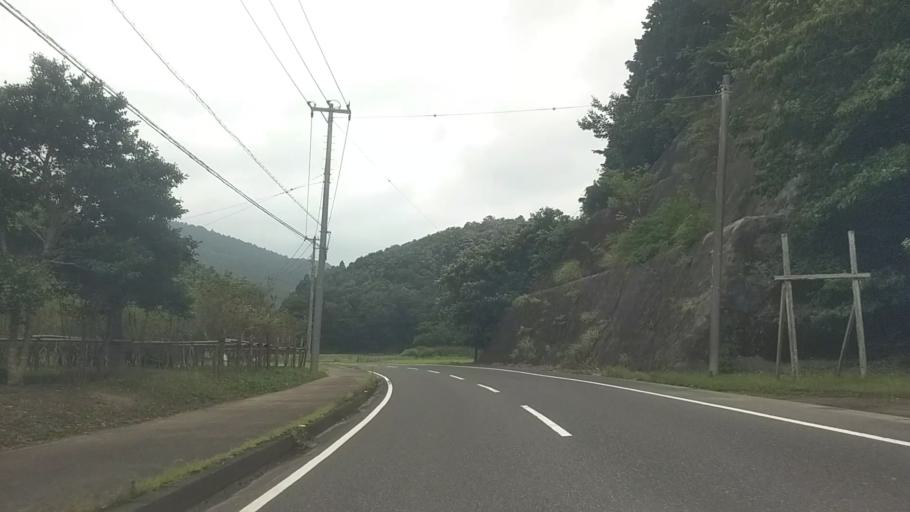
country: JP
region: Chiba
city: Kawaguchi
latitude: 35.2485
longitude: 140.0391
